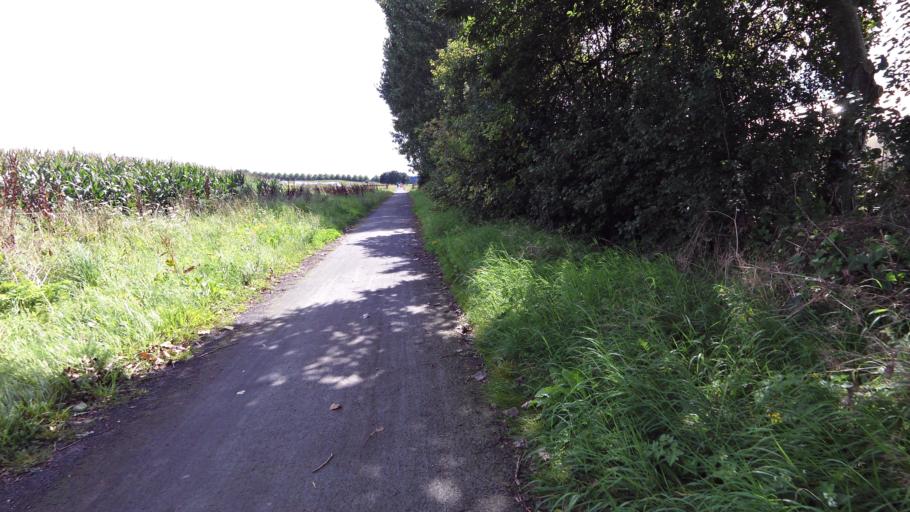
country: BE
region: Flanders
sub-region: Provincie West-Vlaanderen
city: Ichtegem
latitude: 51.1064
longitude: 3.0403
